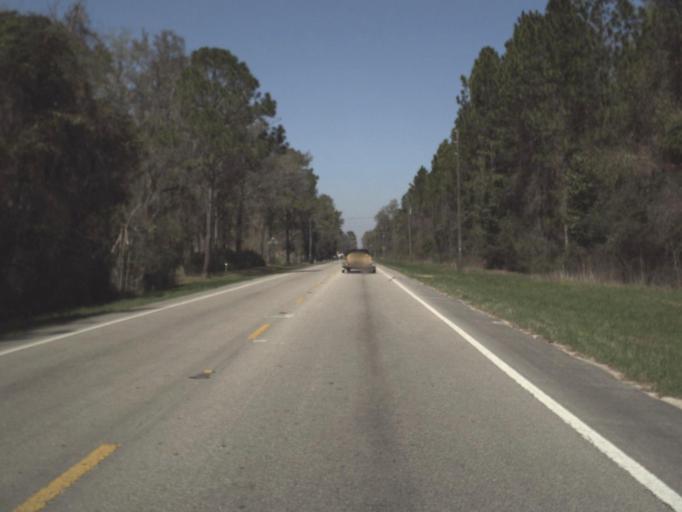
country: US
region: Florida
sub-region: Leon County
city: Woodville
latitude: 30.2390
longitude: -84.2314
